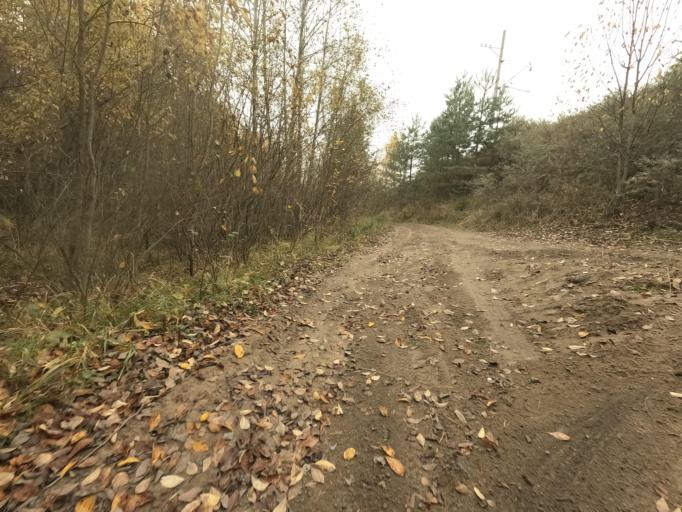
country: RU
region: Leningrad
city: Pavlovo
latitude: 59.7726
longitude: 30.9041
